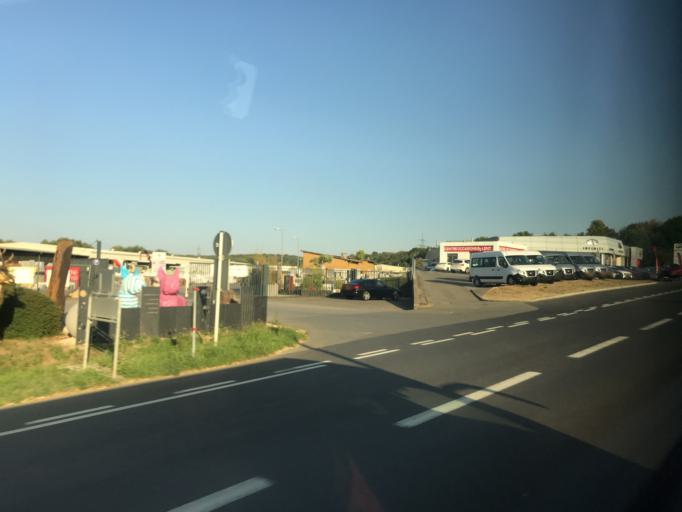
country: LU
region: Luxembourg
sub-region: Canton de Luxembourg
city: Alzingen
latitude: 49.5615
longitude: 6.1651
